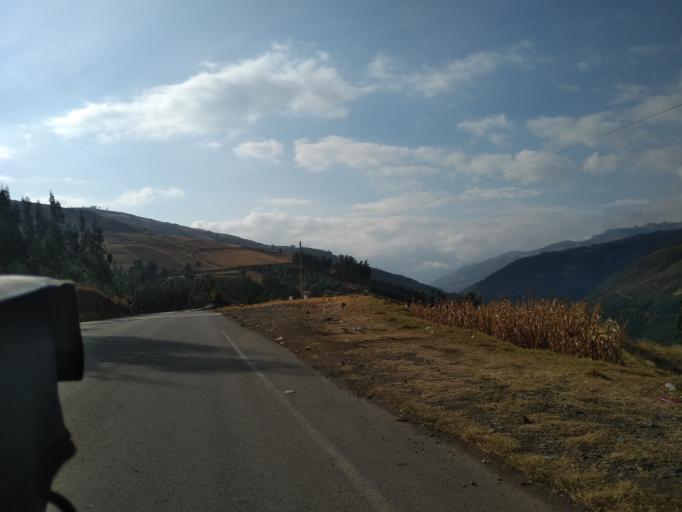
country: PE
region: La Libertad
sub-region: Provincia de Otuzco
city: Agallpampa
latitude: -7.9955
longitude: -78.5263
